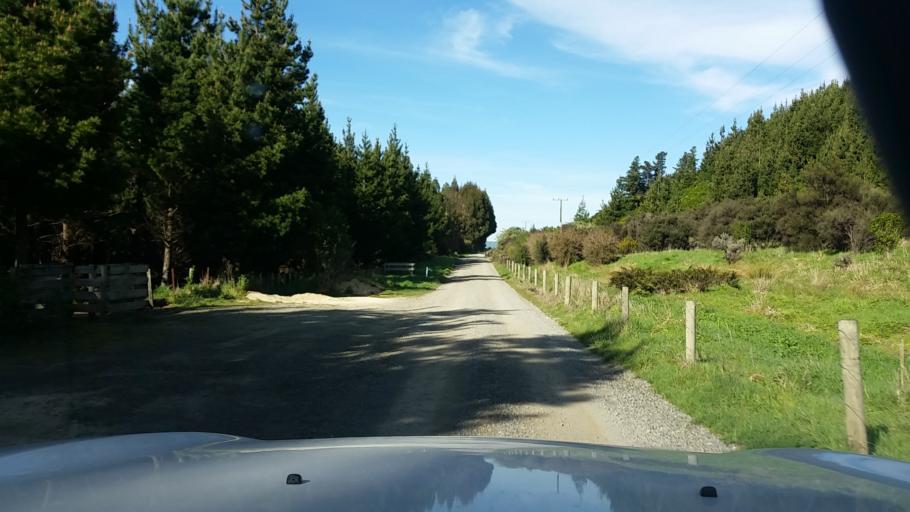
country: NZ
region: Wellington
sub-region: Masterton District
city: Masterton
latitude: -41.0035
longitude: 175.4531
